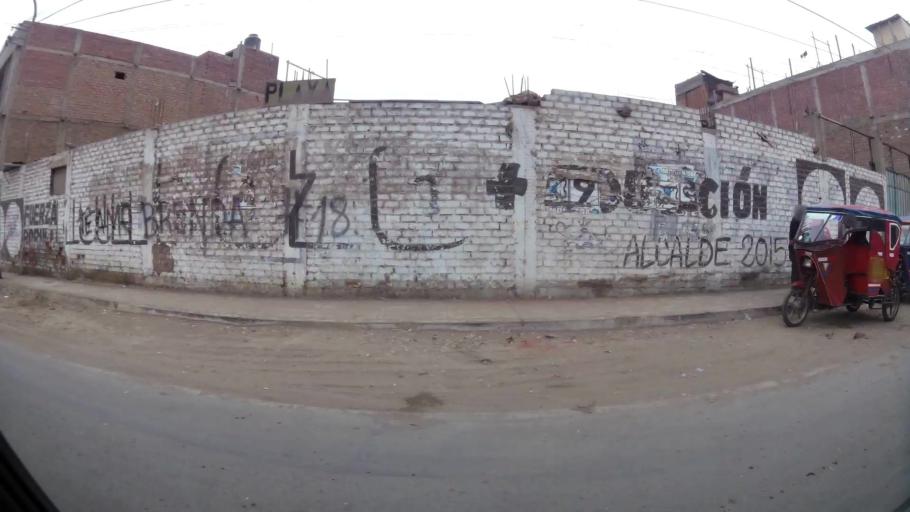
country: PE
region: Lima
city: Ventanilla
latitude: -11.9278
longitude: -77.0776
